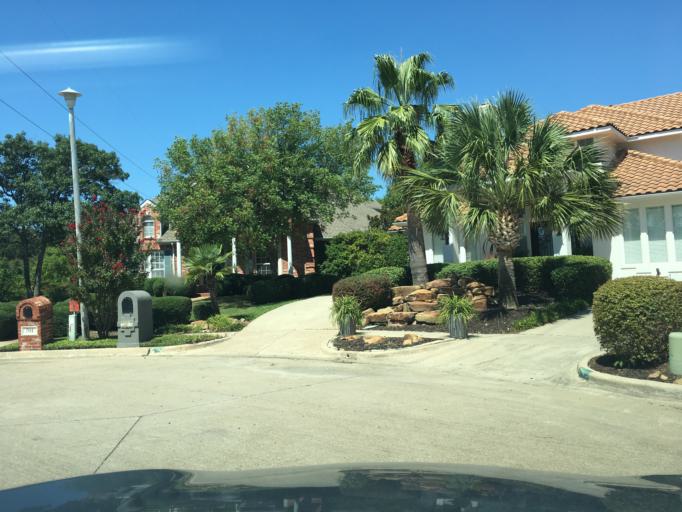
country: US
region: Texas
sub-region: Dallas County
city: Sachse
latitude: 32.9647
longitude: -96.6230
